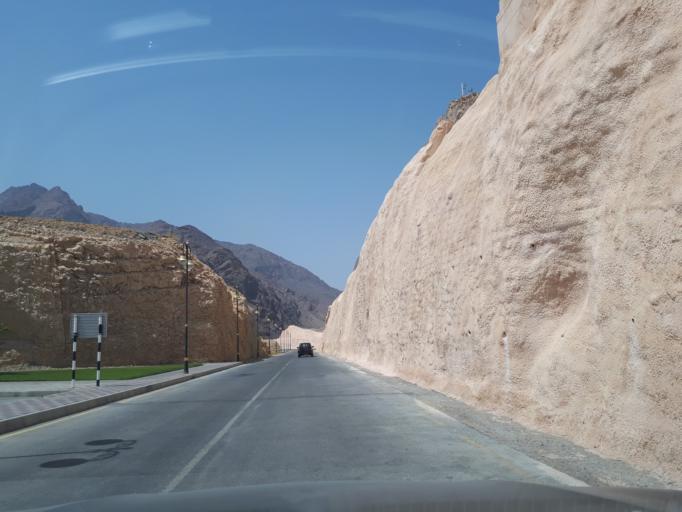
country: OM
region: Ash Sharqiyah
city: Ibra'
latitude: 23.0861
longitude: 58.8483
